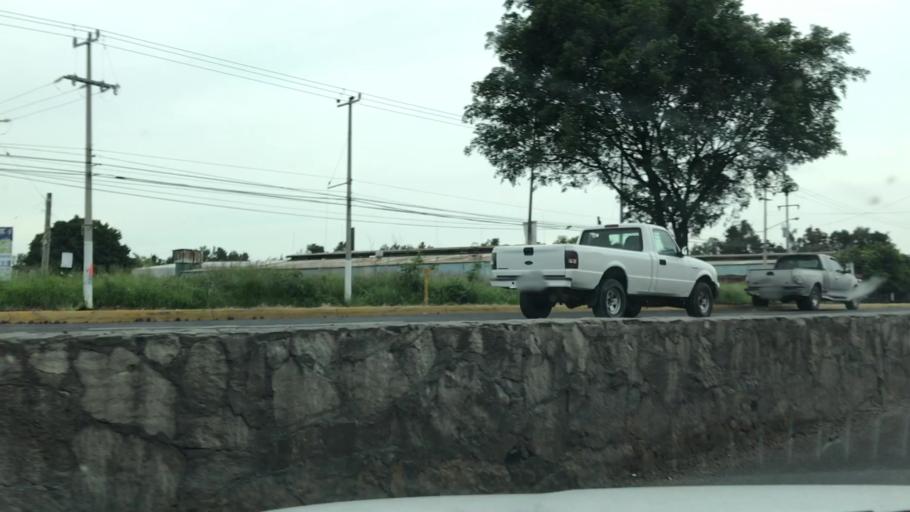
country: MX
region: Jalisco
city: Nuevo Mexico
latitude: 20.7540
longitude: -103.4252
